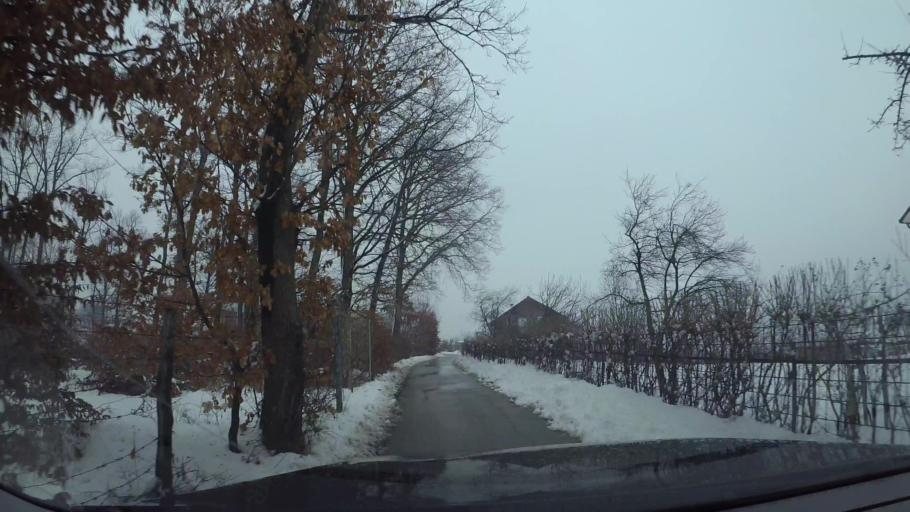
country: BA
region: Federation of Bosnia and Herzegovina
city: Hadzici
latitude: 43.8470
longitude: 18.2711
